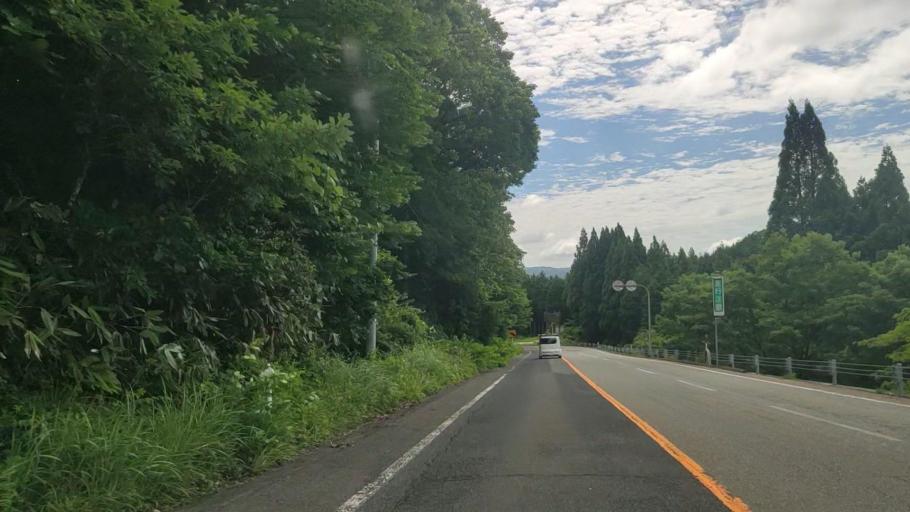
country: JP
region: Okayama
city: Niimi
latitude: 35.1819
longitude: 133.5437
